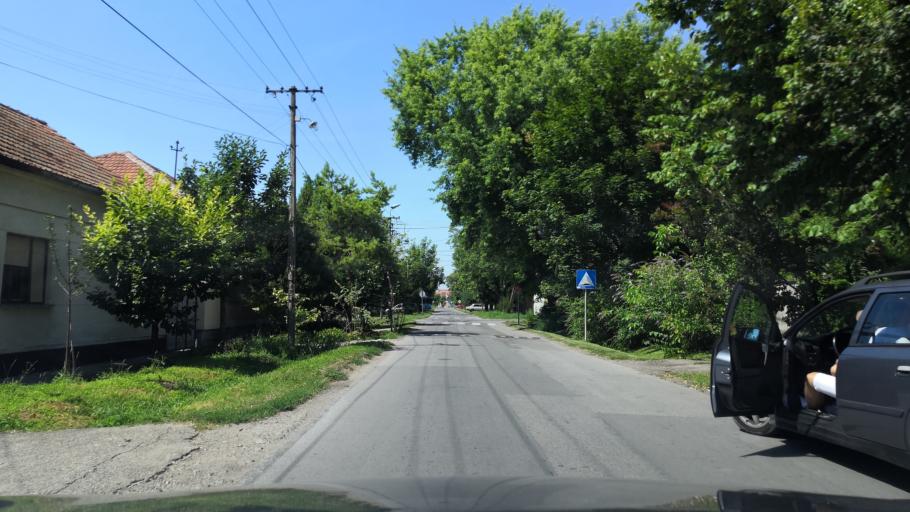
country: RS
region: Autonomna Pokrajina Vojvodina
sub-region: Sremski Okrug
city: Stara Pazova
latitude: 44.9848
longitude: 20.1430
